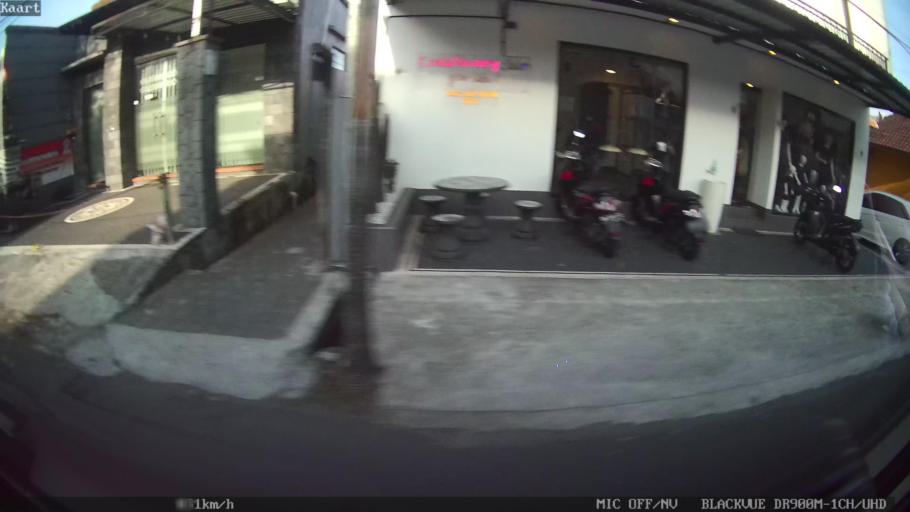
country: ID
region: Bali
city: Banjar Batur
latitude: -8.6071
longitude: 115.2136
